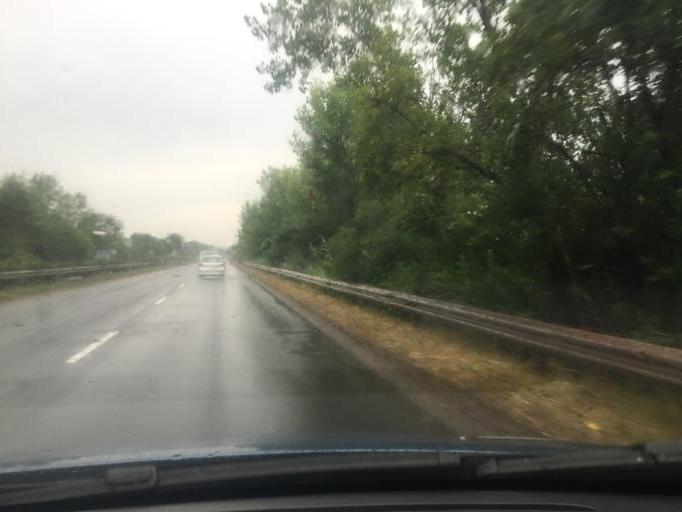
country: BG
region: Burgas
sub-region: Obshtina Burgas
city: Burgas
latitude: 42.5365
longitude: 27.4715
